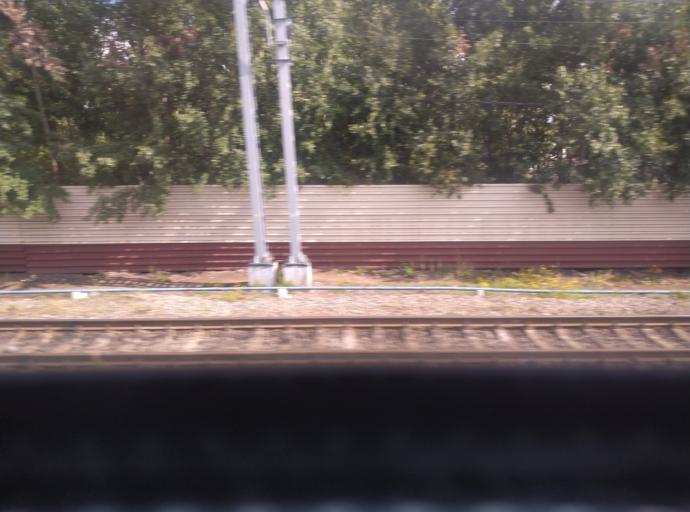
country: RU
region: St.-Petersburg
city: Kolpino
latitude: 59.7538
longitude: 30.6084
